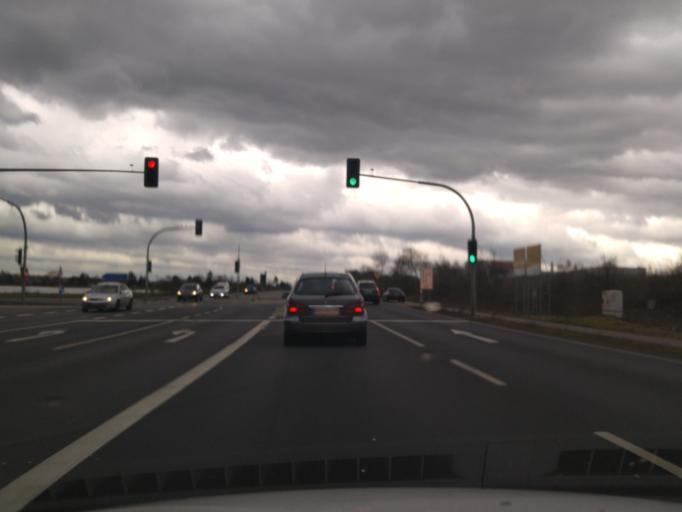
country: DE
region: North Rhine-Westphalia
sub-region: Regierungsbezirk Dusseldorf
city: Dusseldorf
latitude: 51.1629
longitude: 6.7691
